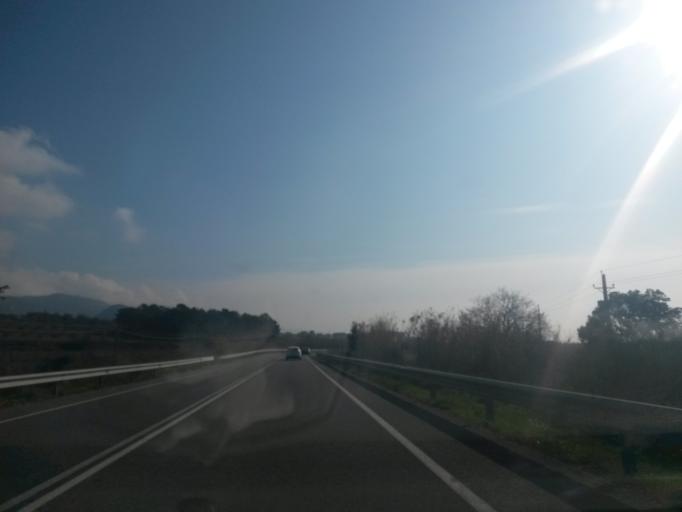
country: ES
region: Catalonia
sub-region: Provincia de Girona
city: Vilajuiga
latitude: 42.3310
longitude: 3.0846
